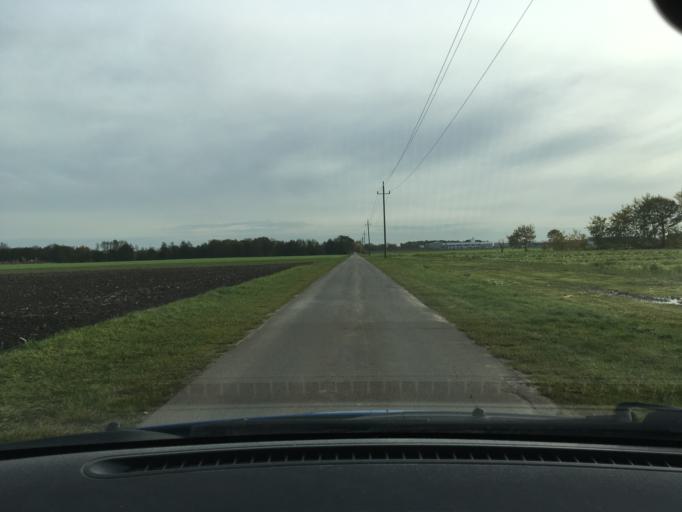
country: DE
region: Lower Saxony
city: Wittorf
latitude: 53.3222
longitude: 10.3711
